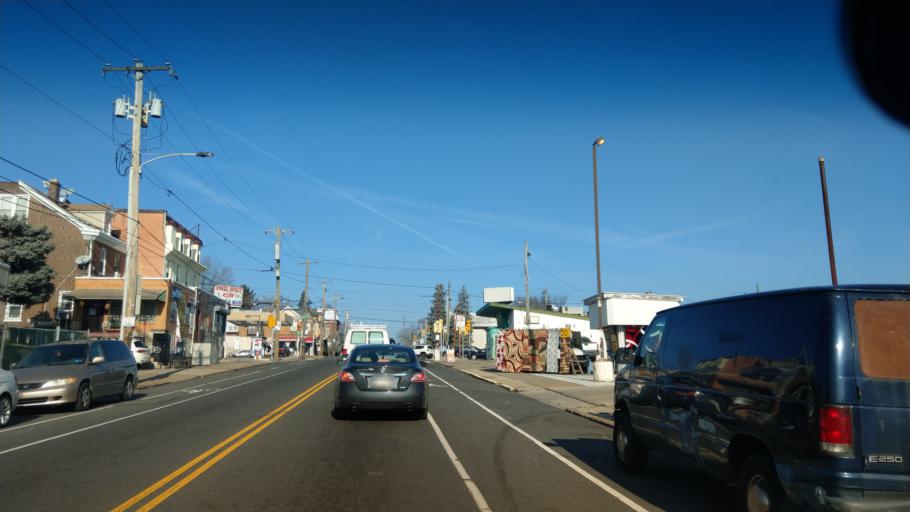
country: US
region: Pennsylvania
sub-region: Montgomery County
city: Rockledge
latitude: 40.0296
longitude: -75.1189
